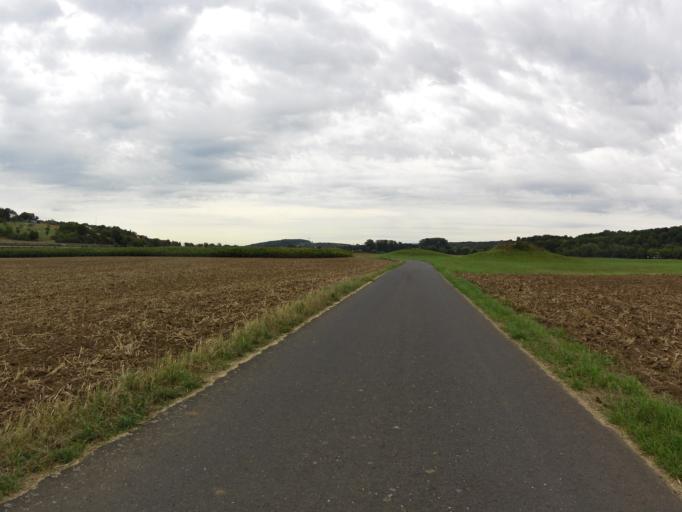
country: DE
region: Bavaria
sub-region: Regierungsbezirk Unterfranken
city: Gadheim
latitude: 50.0248
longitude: 10.3290
